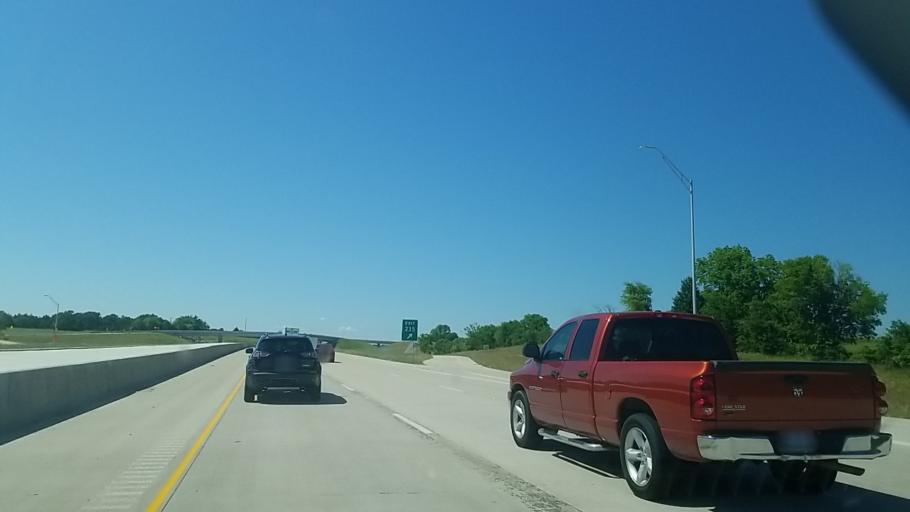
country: US
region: Texas
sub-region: Navarro County
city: Corsicana
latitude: 32.1481
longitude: -96.4650
